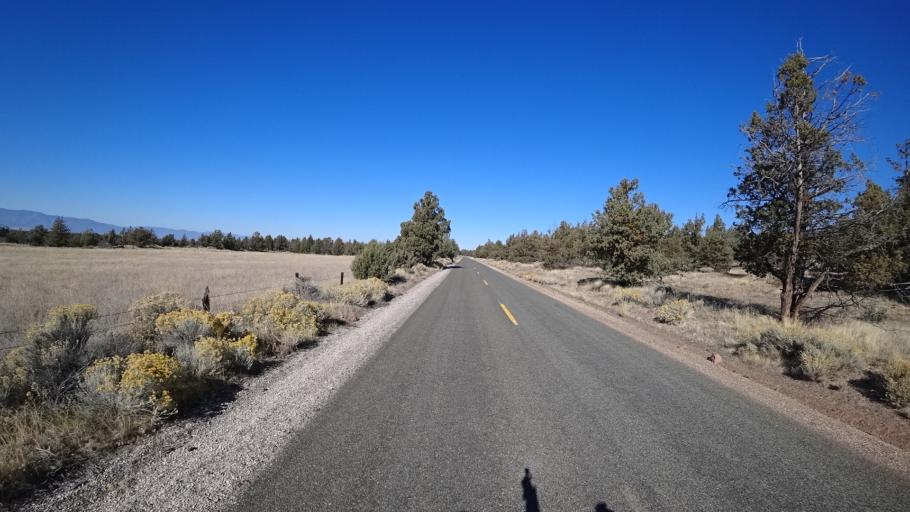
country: US
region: California
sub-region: Siskiyou County
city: Weed
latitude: 41.6079
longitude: -122.3099
